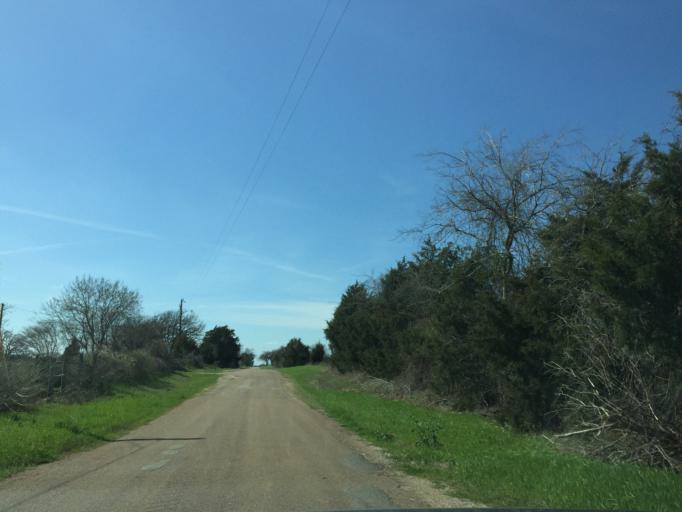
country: US
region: Texas
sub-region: Milam County
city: Thorndale
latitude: 30.5736
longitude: -97.1606
